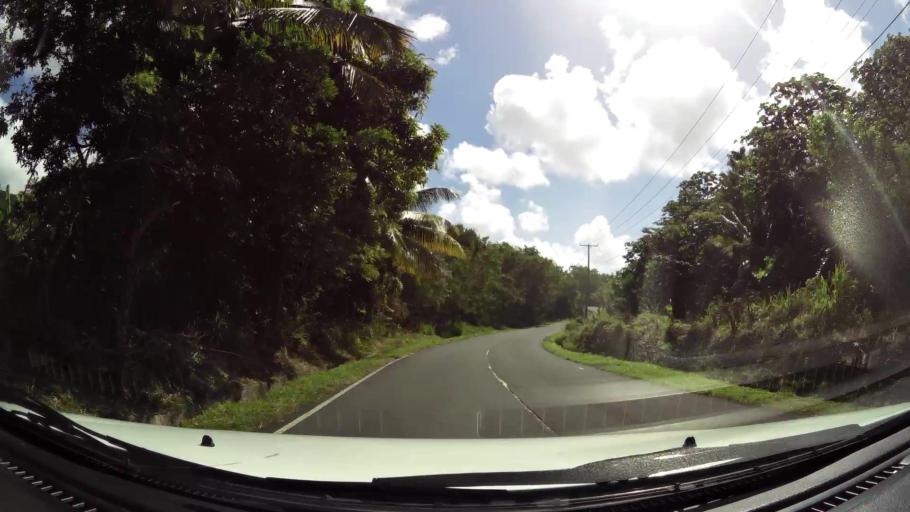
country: LC
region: Laborie Quarter
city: Laborie
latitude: 13.7561
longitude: -61.0133
